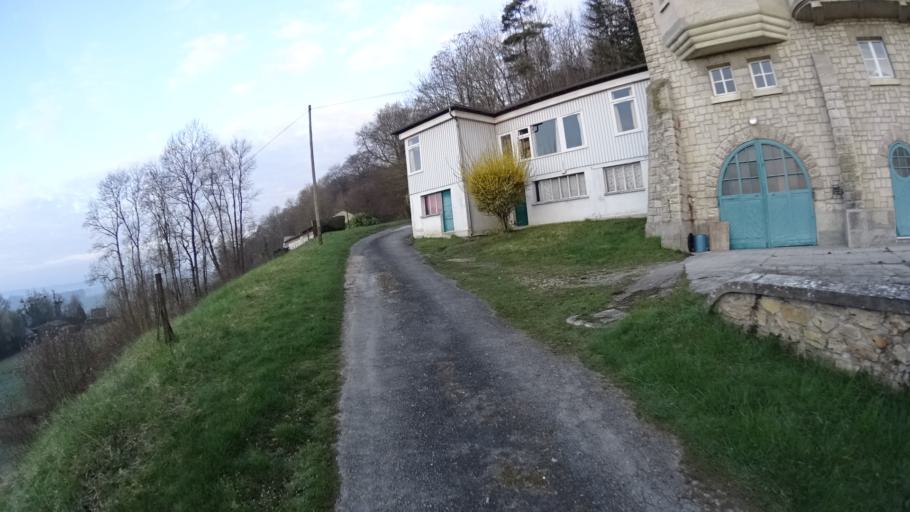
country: FR
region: Picardie
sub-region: Departement de l'Aisne
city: Vic-sur-Aisne
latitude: 49.4375
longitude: 3.1298
